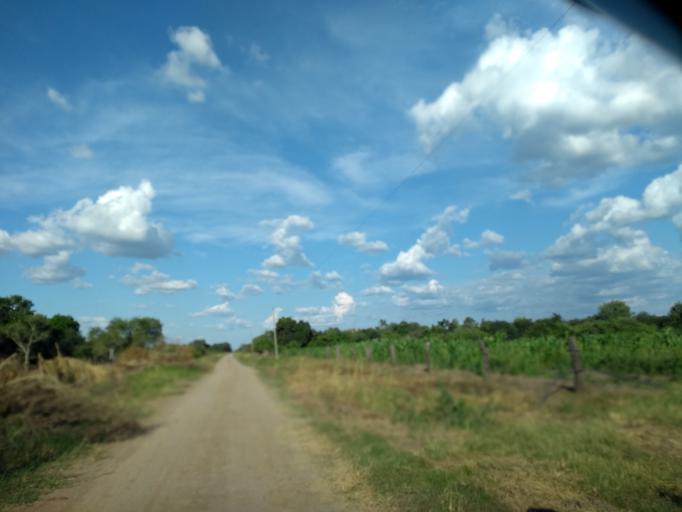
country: AR
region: Chaco
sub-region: Departamento de Quitilipi
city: Quitilipi
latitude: -26.7459
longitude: -60.2747
